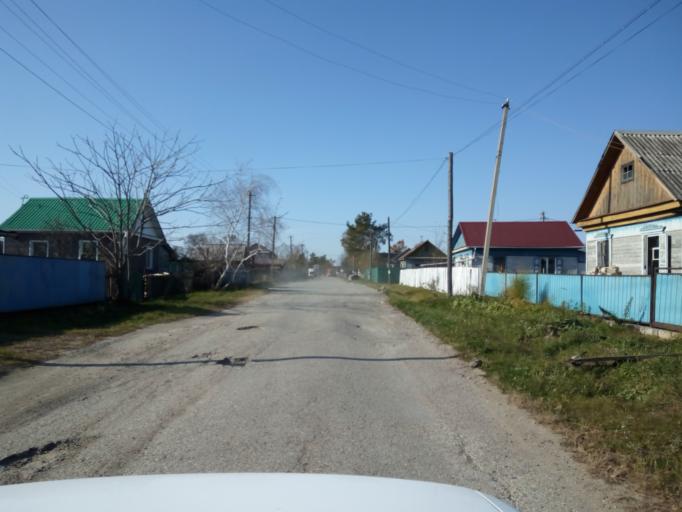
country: RU
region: Primorskiy
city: Dal'nerechensk
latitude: 45.9242
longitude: 133.7244
